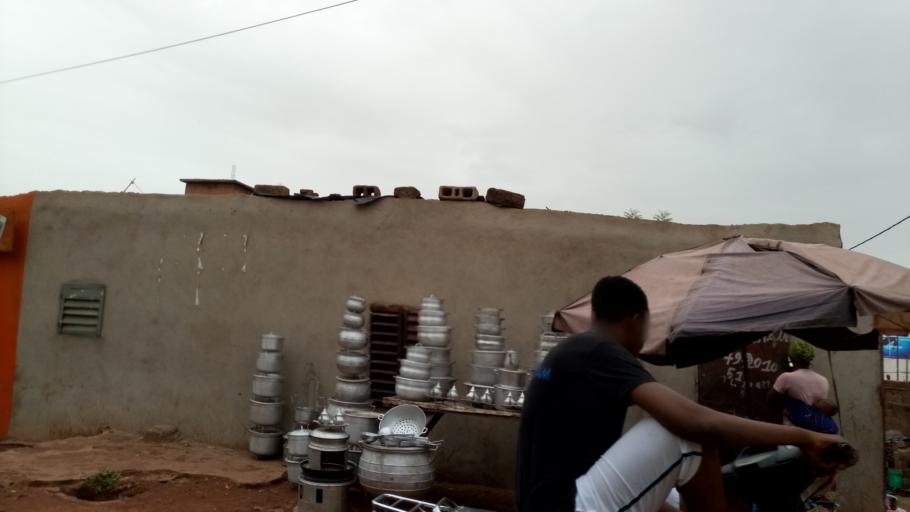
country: ML
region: Bamako
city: Bamako
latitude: 12.5886
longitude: -7.9917
